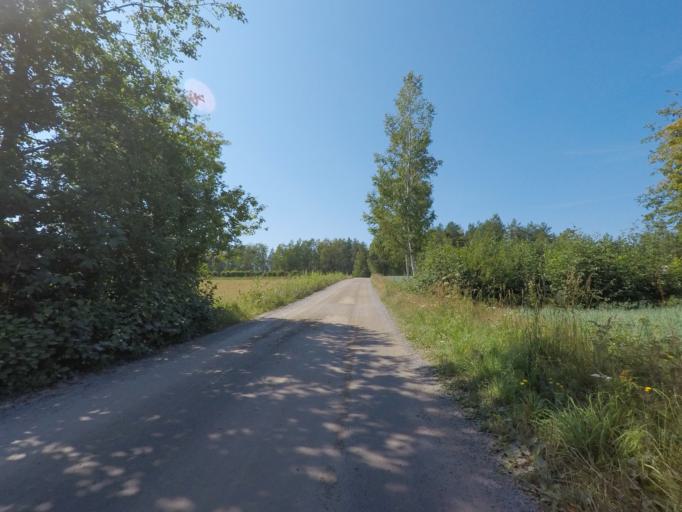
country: FI
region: Southern Savonia
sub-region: Mikkeli
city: Puumala
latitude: 61.4278
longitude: 28.0258
